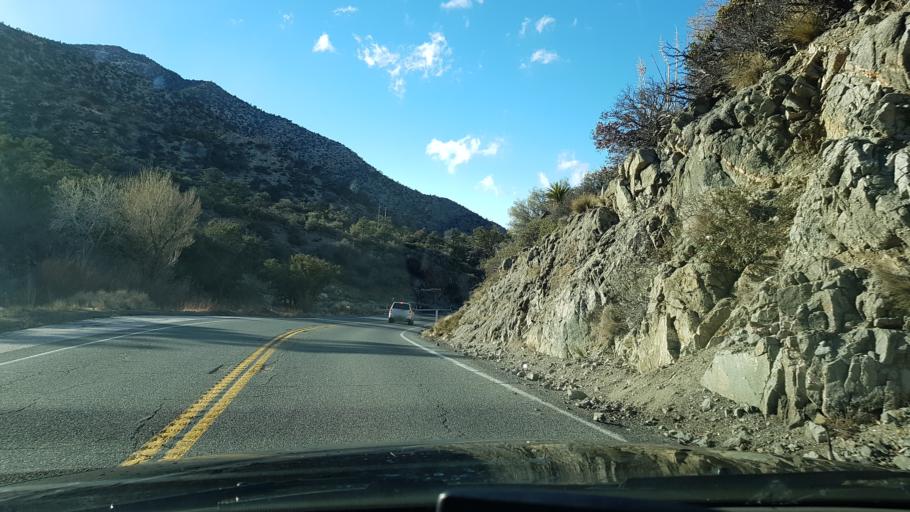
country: US
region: California
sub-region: San Bernardino County
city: Big Bear City
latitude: 34.3347
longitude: -116.8327
